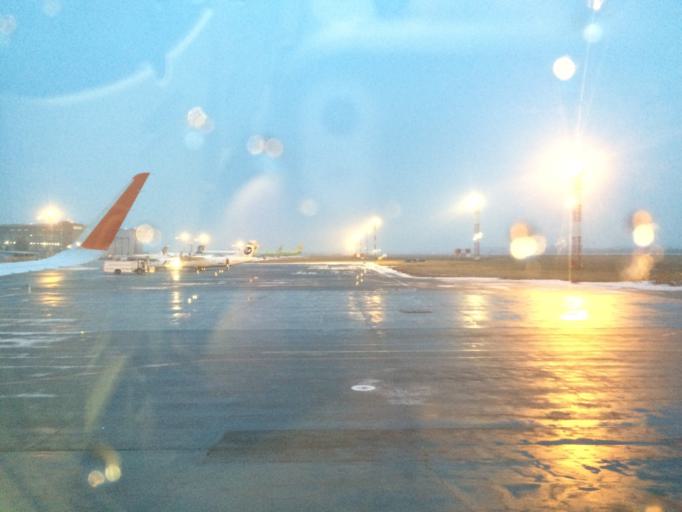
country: RU
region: Novosibirsk
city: Ob'
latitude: 55.0111
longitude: 82.6654
